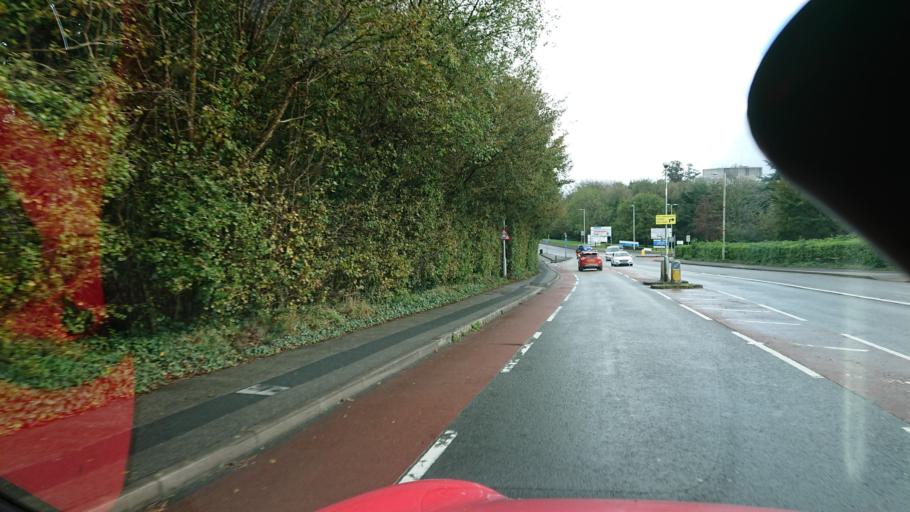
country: GB
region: England
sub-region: Plymouth
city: Plymouth
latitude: 50.4189
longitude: -4.1177
